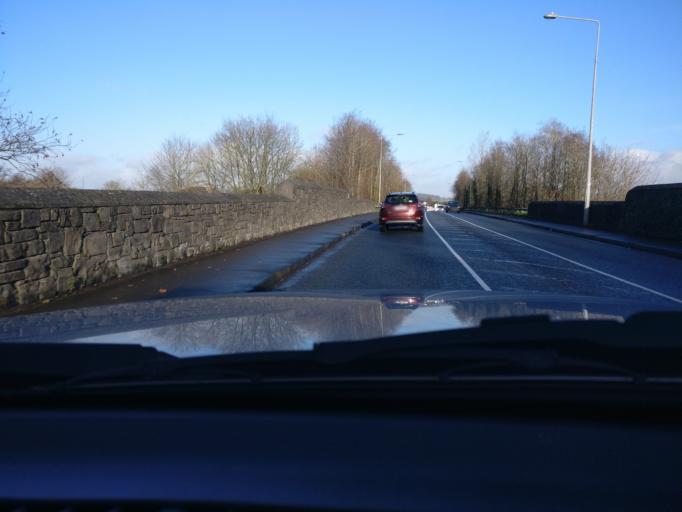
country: IE
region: Leinster
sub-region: An Iarmhi
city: An Muileann gCearr
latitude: 53.5371
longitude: -7.3476
